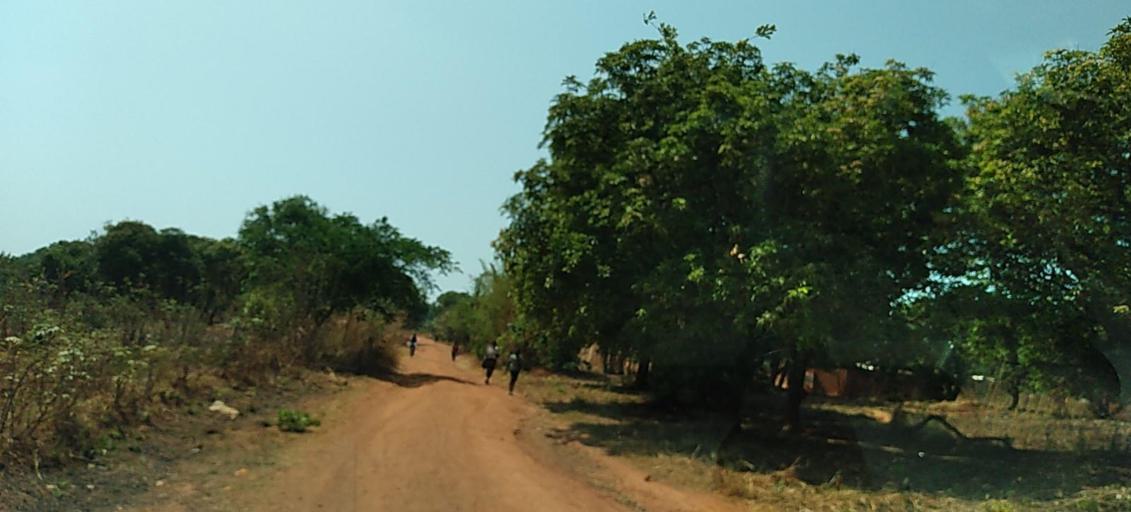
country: ZM
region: Copperbelt
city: Luanshya
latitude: -13.3504
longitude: 28.4051
